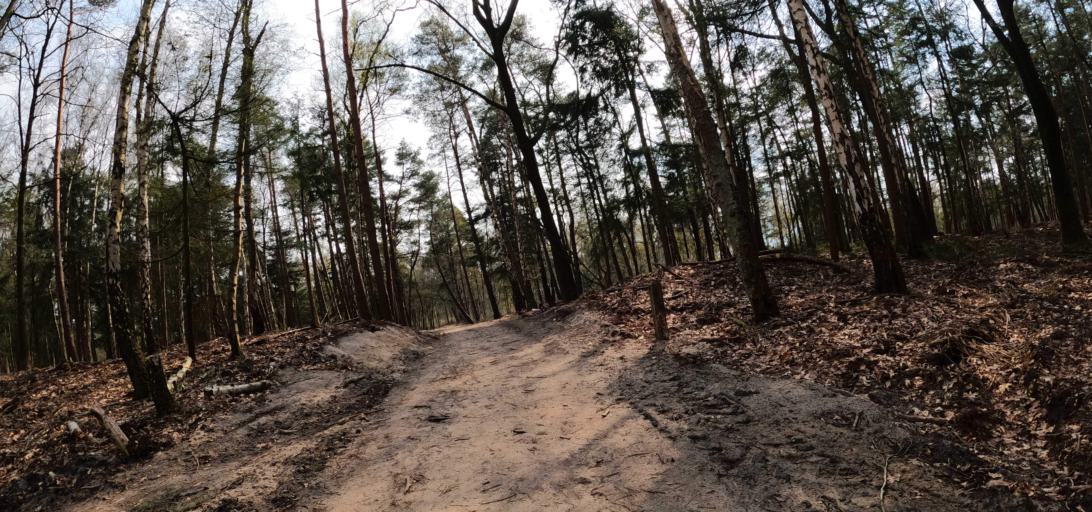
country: BE
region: Flanders
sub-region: Provincie Antwerpen
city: Kalmthout
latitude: 51.4157
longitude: 4.4540
